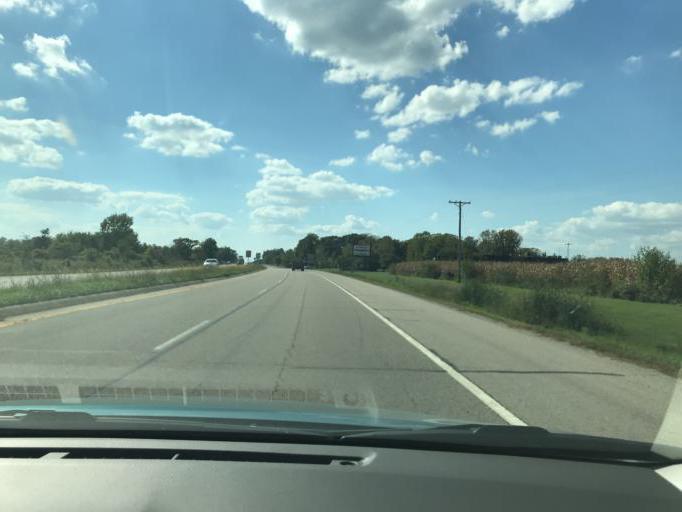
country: US
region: Wisconsin
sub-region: Walworth County
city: Como
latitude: 42.5899
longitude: -88.4631
